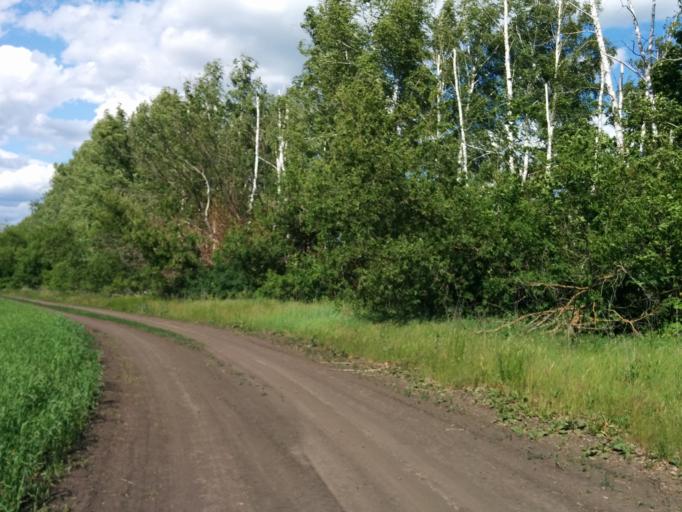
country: RU
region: Tambov
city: Tambov
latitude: 52.7987
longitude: 41.3849
